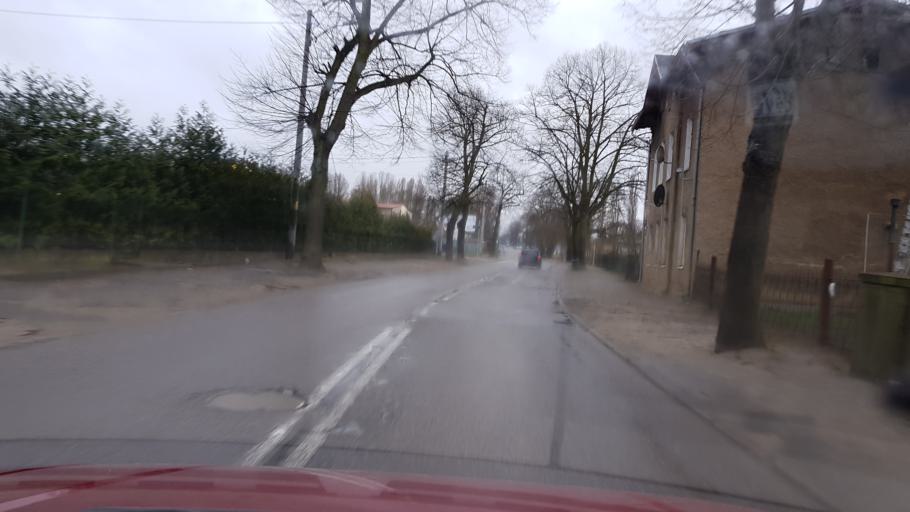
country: PL
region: West Pomeranian Voivodeship
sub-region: Szczecin
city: Szczecin
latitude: 53.3538
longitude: 14.5788
